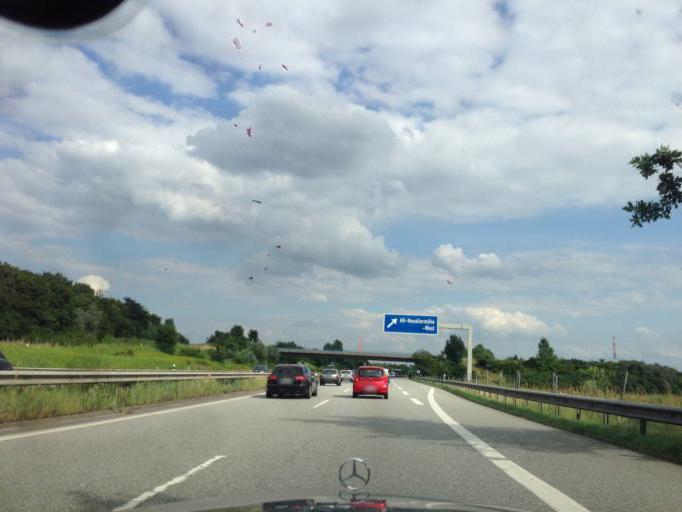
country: DE
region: Schleswig-Holstein
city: Oststeinbek
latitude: 53.4817
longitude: 10.1465
